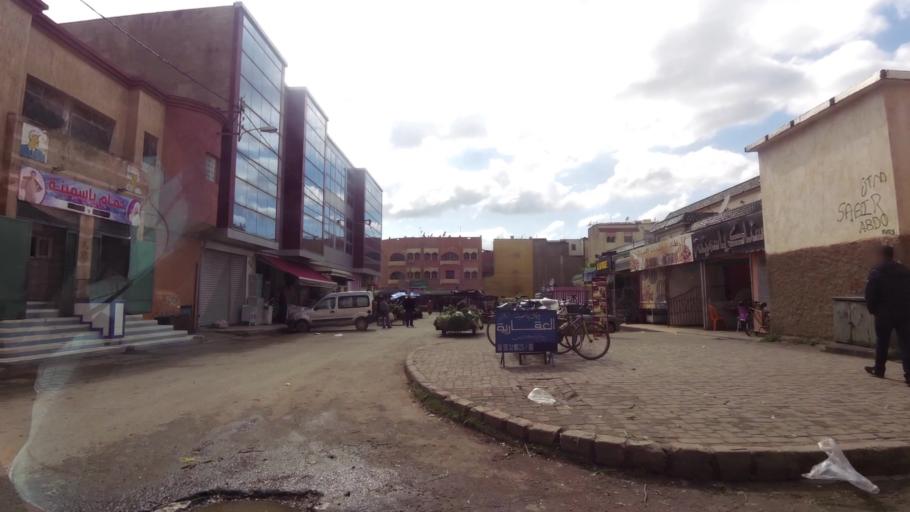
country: MA
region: Chaouia-Ouardigha
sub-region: Settat Province
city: Berrechid
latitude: 33.2649
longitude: -7.5758
